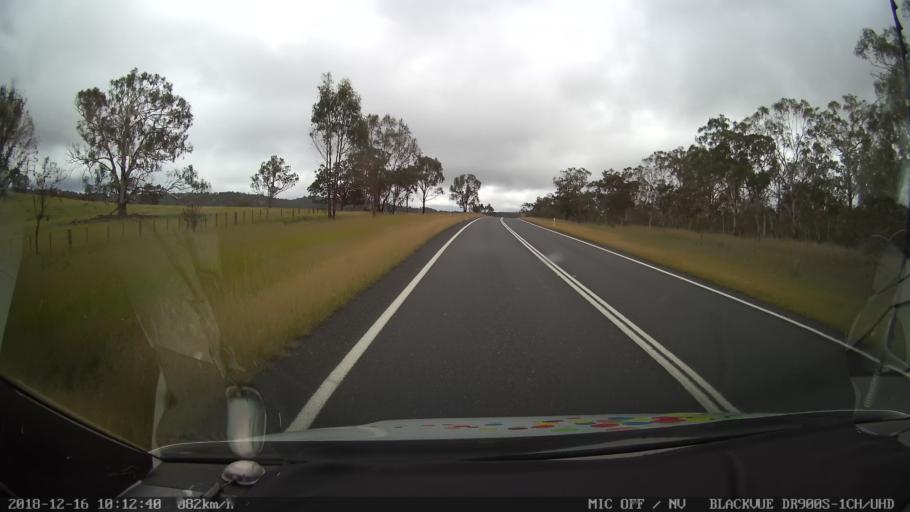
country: AU
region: New South Wales
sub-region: Glen Innes Severn
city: Glen Innes
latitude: -29.3041
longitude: 151.9433
